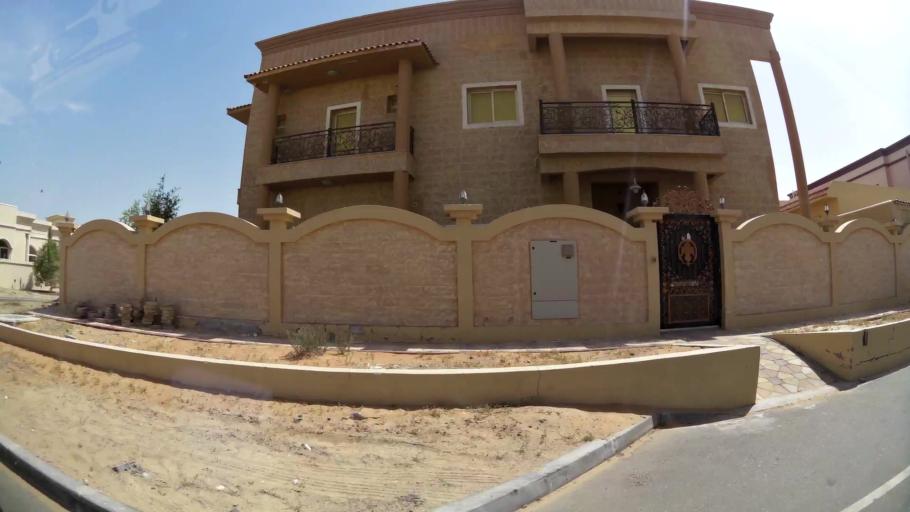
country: AE
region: Ash Shariqah
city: Sharjah
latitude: 25.1925
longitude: 55.4381
